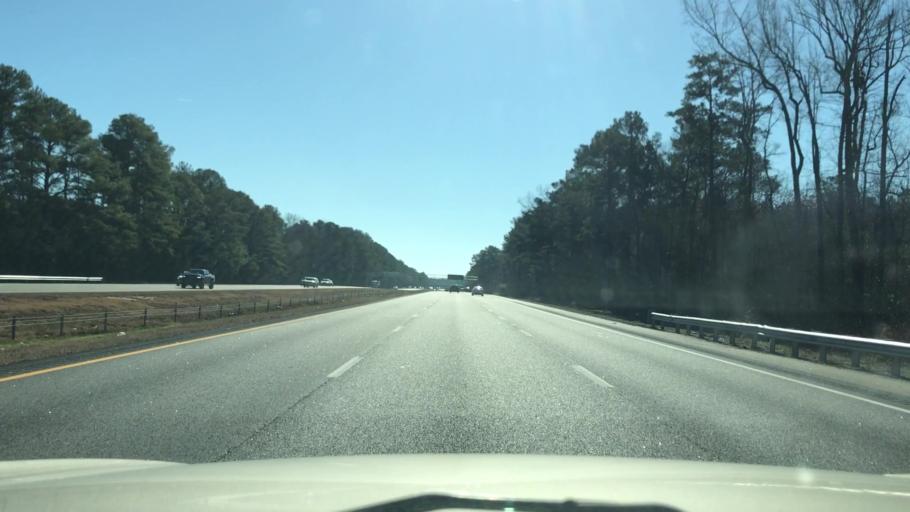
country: US
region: South Carolina
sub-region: Lexington County
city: Pineridge
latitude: 33.9020
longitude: -81.0494
